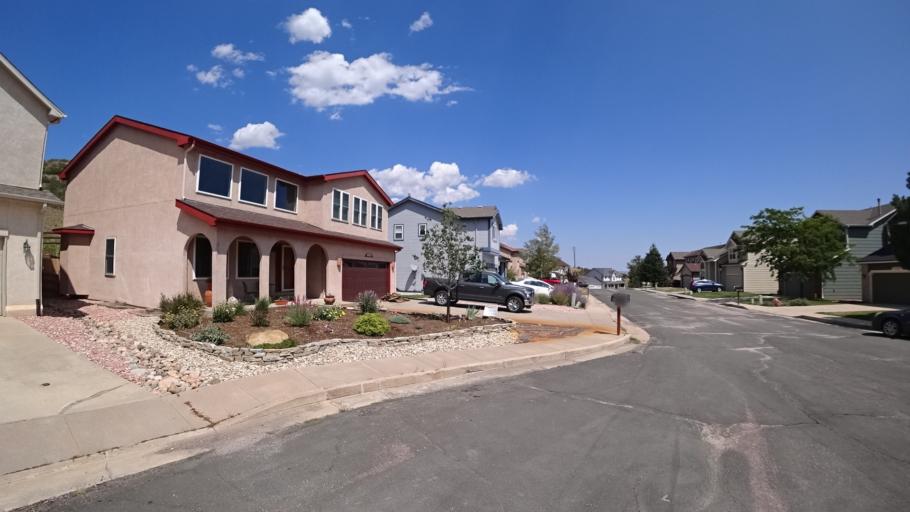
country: US
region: Colorado
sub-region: El Paso County
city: Air Force Academy
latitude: 38.9394
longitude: -104.8811
